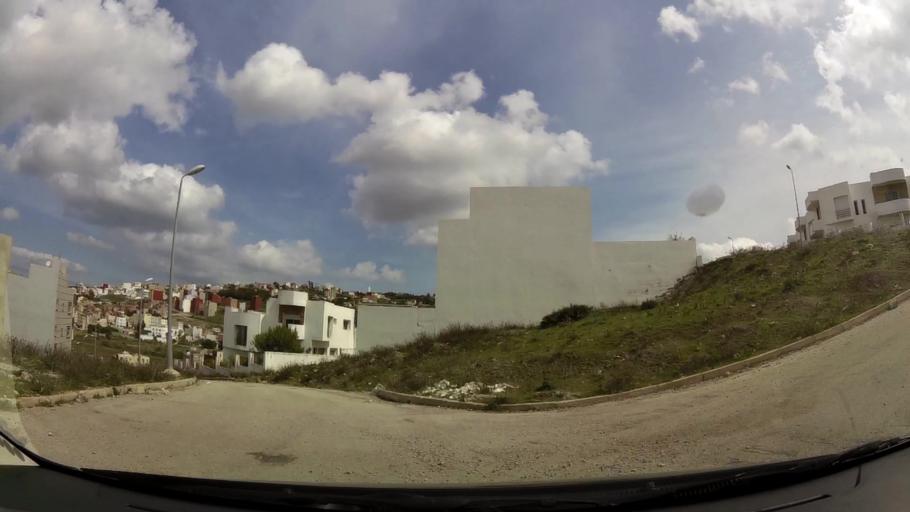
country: MA
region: Tanger-Tetouan
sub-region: Tanger-Assilah
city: Tangier
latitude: 35.7644
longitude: -5.7550
